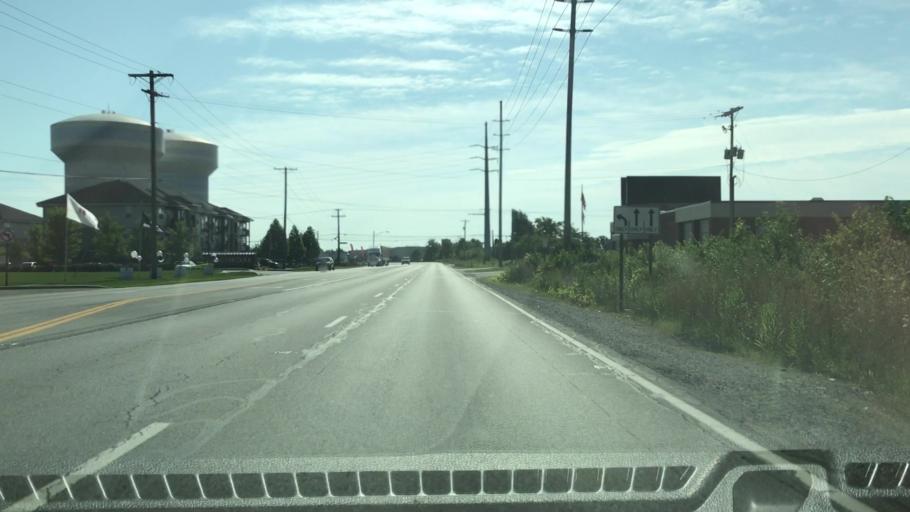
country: US
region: Ohio
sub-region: Franklin County
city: Lincoln Village
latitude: 39.9730
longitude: -83.1486
